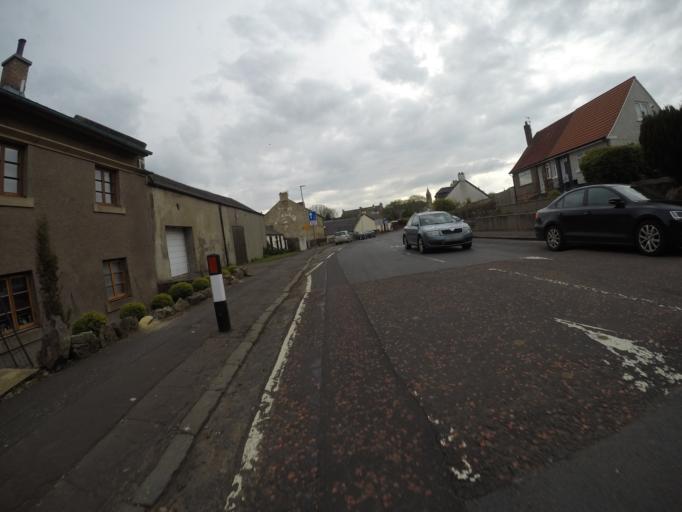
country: GB
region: Scotland
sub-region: East Ayrshire
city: Kilmaurs
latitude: 55.6386
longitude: -4.5243
